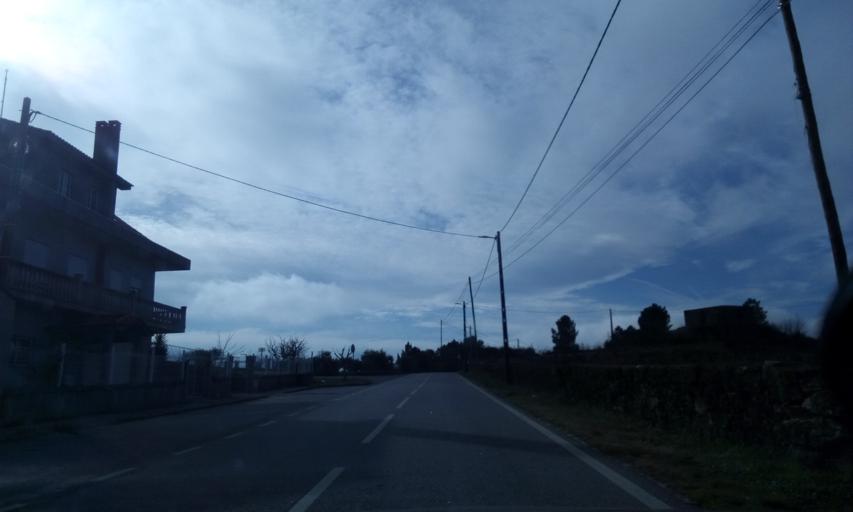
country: PT
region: Guarda
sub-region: Aguiar da Beira
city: Aguiar da Beira
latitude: 40.7582
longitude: -7.5429
